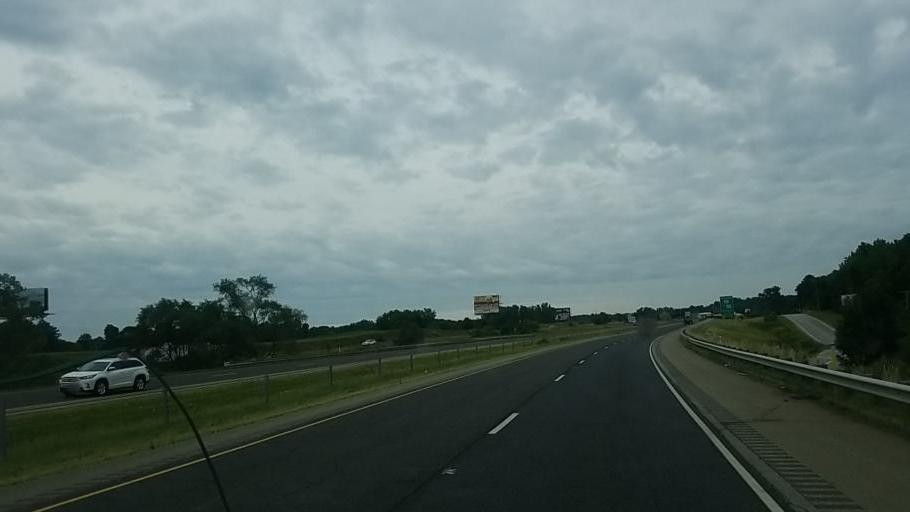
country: US
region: Indiana
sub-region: Steuben County
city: Fremont
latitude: 41.7204
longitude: -85.0010
